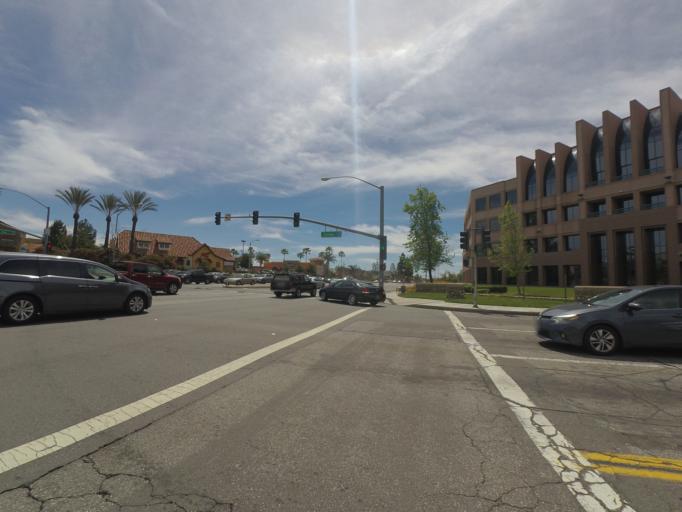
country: US
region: California
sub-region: Riverside County
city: March Air Force Base
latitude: 33.9377
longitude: -117.2791
